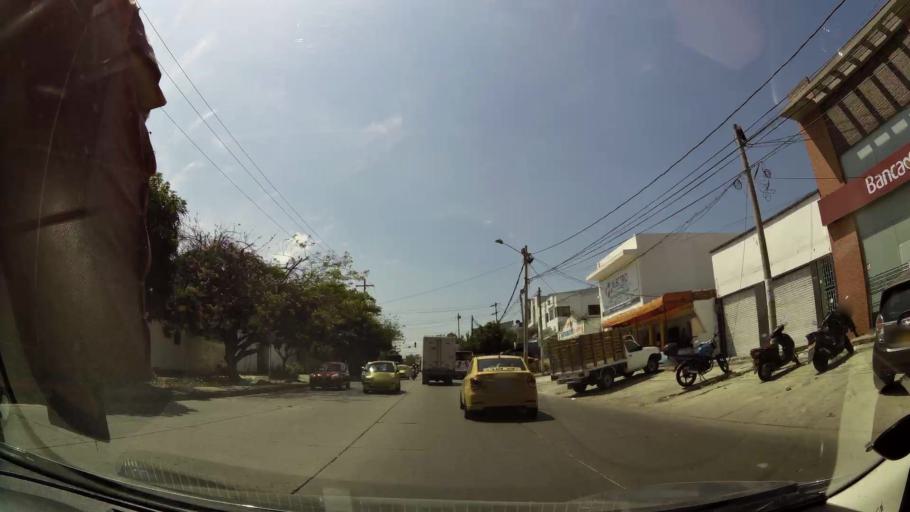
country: CO
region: Atlantico
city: Barranquilla
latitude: 10.9591
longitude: -74.8027
